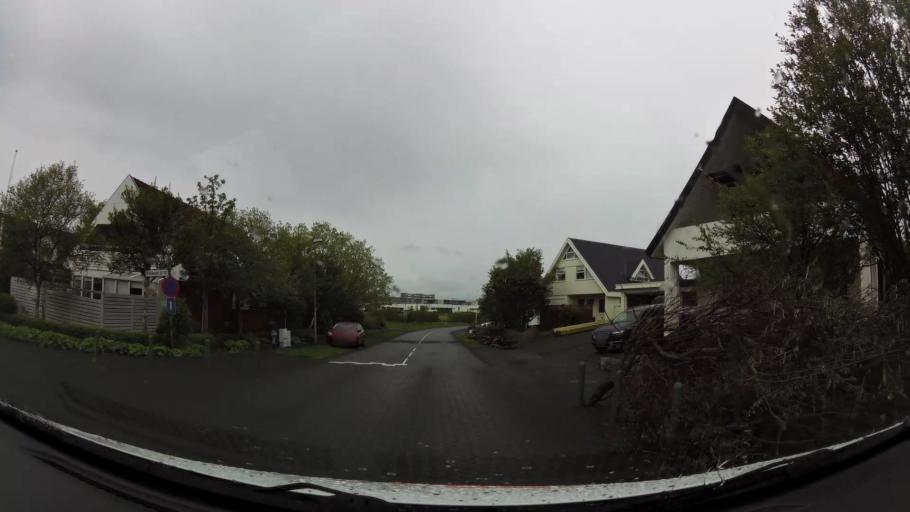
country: IS
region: Capital Region
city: Gardabaer
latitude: 64.0937
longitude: -21.9150
